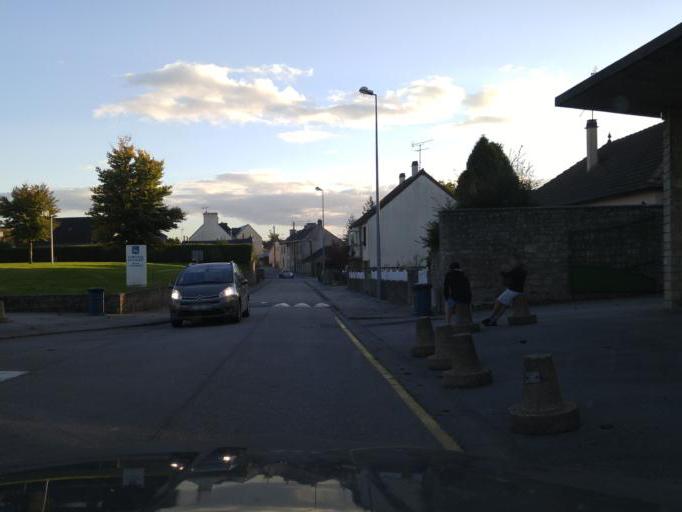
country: FR
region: Lower Normandy
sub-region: Departement de la Manche
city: Valognes
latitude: 49.5136
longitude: -1.4713
